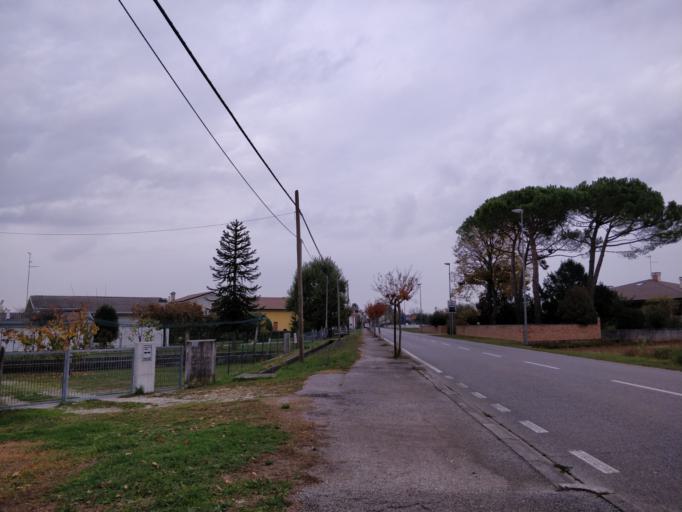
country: IT
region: Friuli Venezia Giulia
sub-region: Provincia di Udine
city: Bertiolo
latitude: 45.9395
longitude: 13.0661
